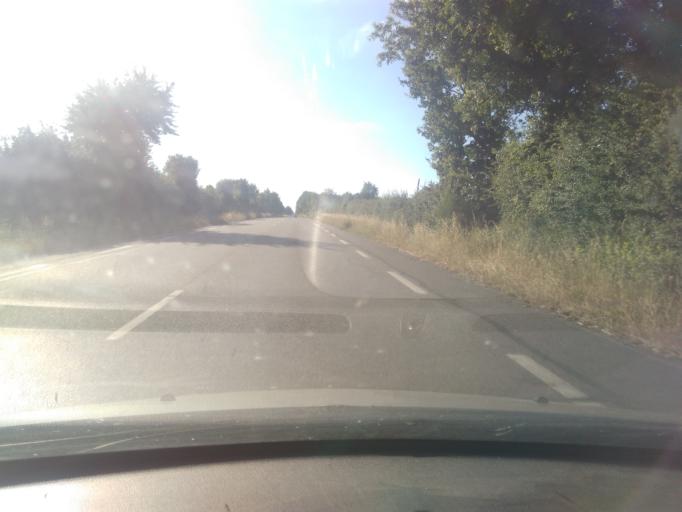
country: FR
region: Pays de la Loire
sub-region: Departement de la Vendee
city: Saint-Florent-des-Bois
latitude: 46.6033
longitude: -1.3329
